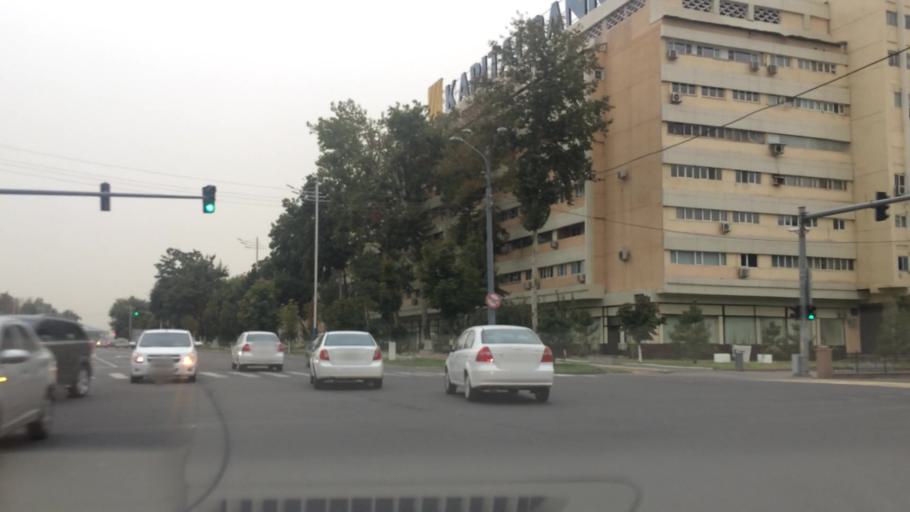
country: UZ
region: Toshkent Shahri
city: Tashkent
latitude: 41.3051
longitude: 69.2658
